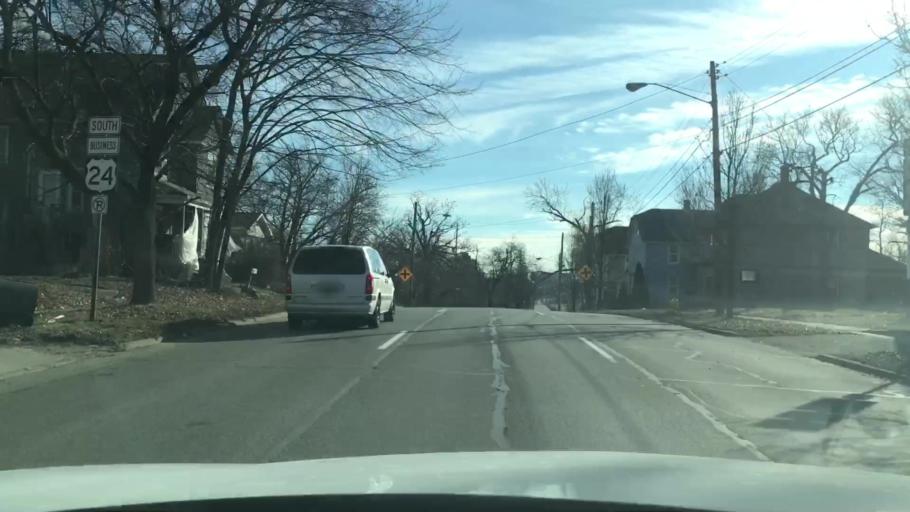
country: US
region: Michigan
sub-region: Oakland County
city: Pontiac
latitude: 42.6443
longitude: -83.3034
